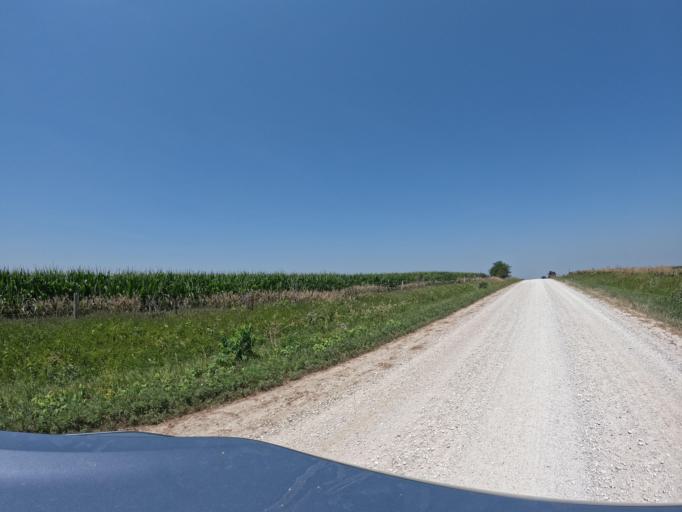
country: US
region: Iowa
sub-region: Keokuk County
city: Sigourney
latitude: 41.2677
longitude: -92.1806
